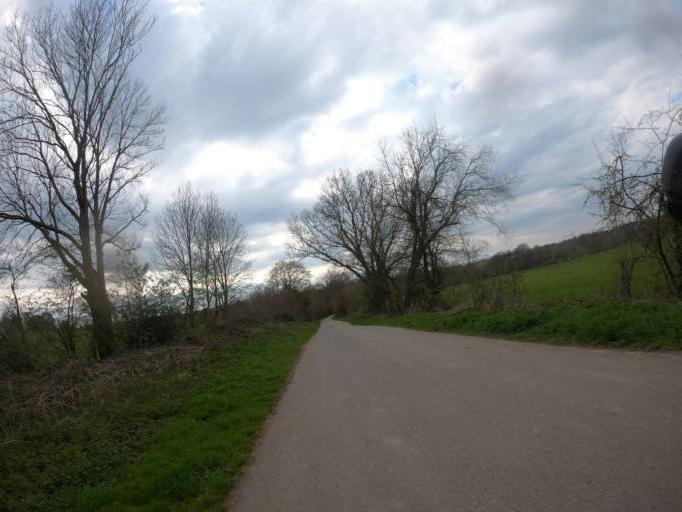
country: DE
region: North Rhine-Westphalia
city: Stolberg
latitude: 50.7305
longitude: 6.1633
